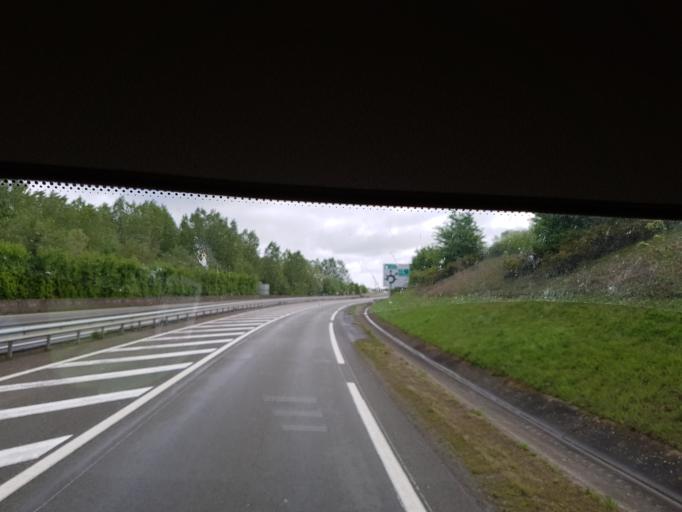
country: FR
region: Picardie
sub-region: Departement de l'Aisne
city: Courmelles
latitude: 49.3579
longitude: 3.3122
